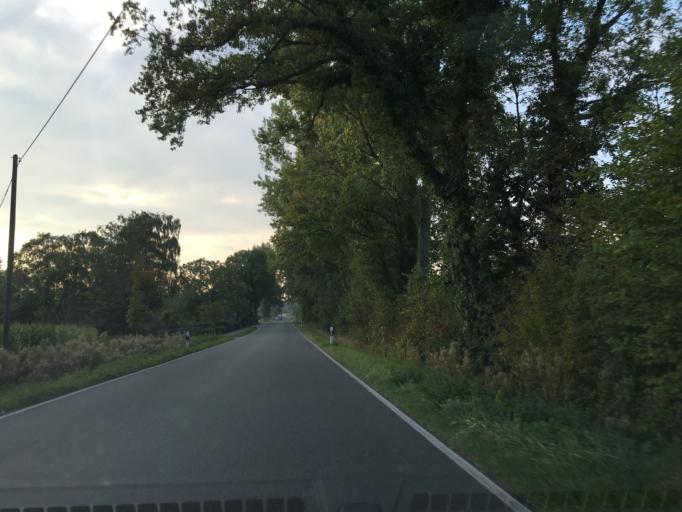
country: DE
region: North Rhine-Westphalia
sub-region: Regierungsbezirk Munster
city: Altenberge
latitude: 52.0435
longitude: 7.4944
